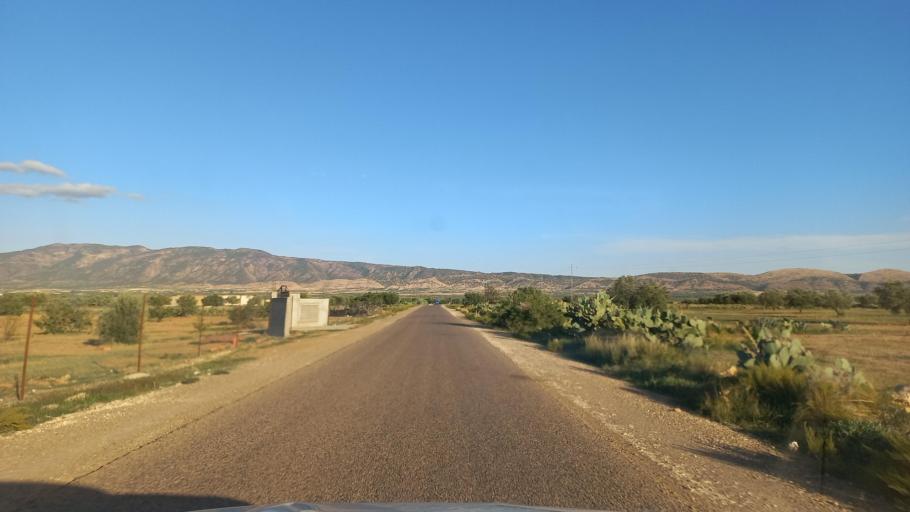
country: TN
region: Al Qasrayn
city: Sbiba
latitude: 35.4126
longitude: 9.1279
